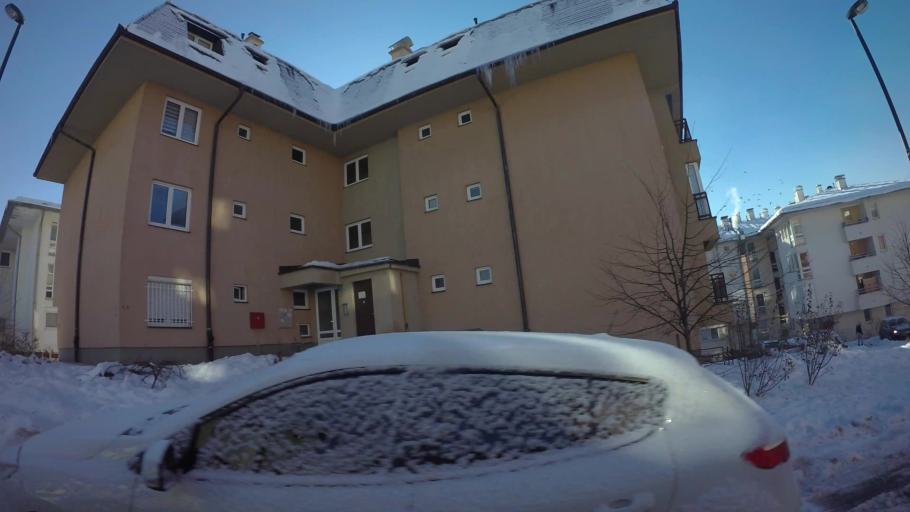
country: BA
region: Federation of Bosnia and Herzegovina
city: Kobilja Glava
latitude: 43.8810
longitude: 18.4000
